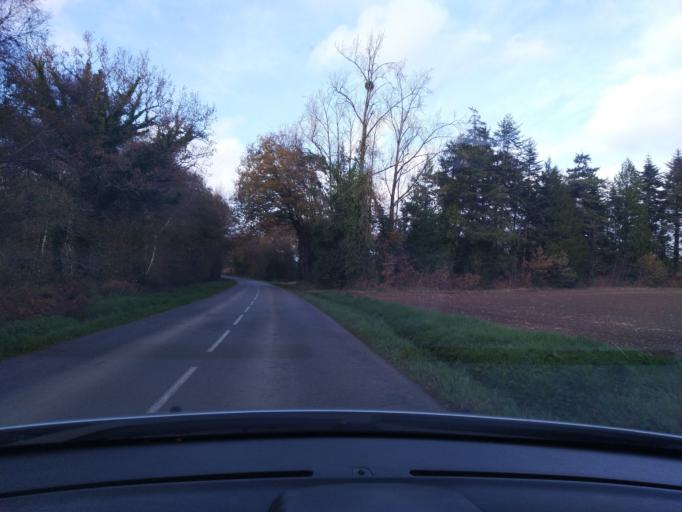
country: FR
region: Brittany
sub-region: Departement du Finistere
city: Plouigneau
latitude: 48.5508
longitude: -3.6855
